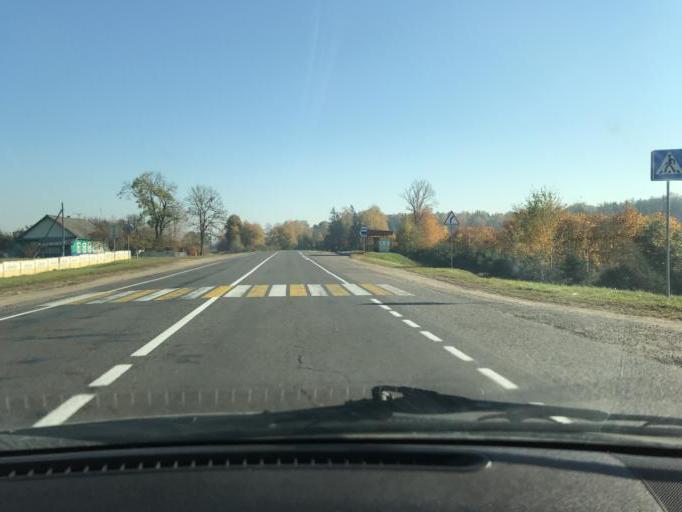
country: BY
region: Brest
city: Lyakhavichy
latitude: 52.9481
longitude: 26.1254
